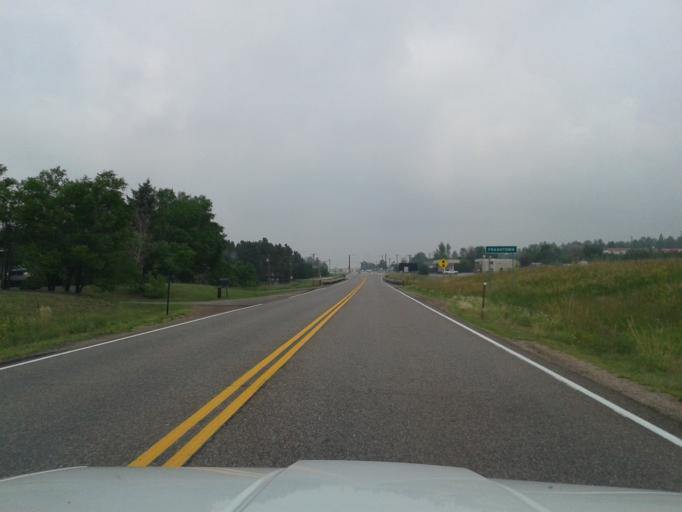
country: US
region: Colorado
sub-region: Douglas County
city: The Pinery
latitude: 39.3871
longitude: -104.7521
